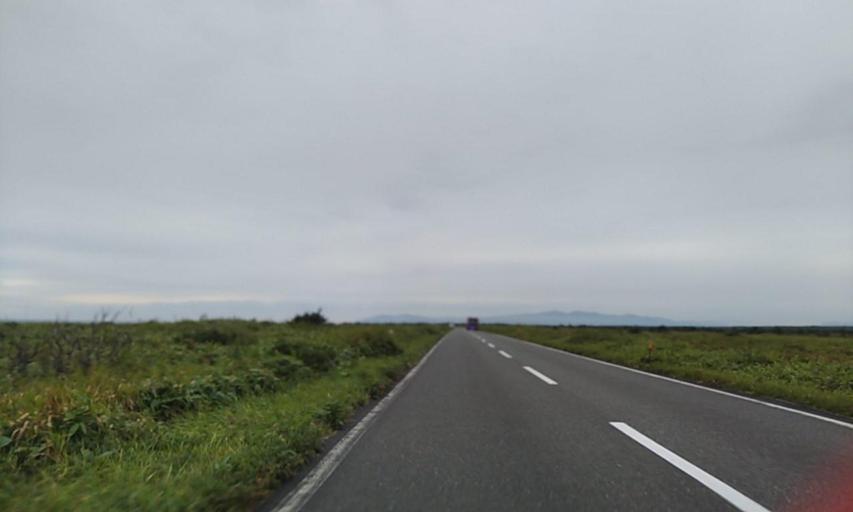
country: JP
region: Hokkaido
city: Makubetsu
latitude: 45.2606
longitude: 142.2460
